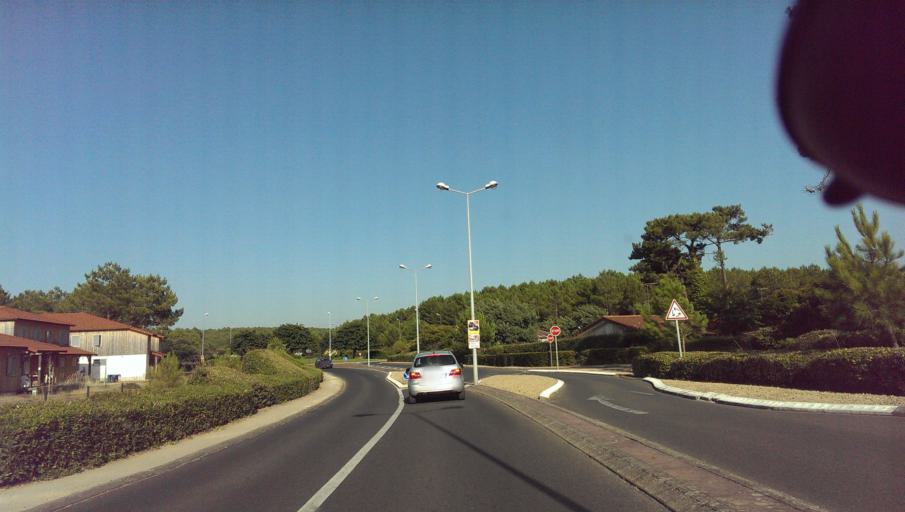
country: FR
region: Aquitaine
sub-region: Departement des Landes
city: Mimizan
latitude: 44.2115
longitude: -1.2848
